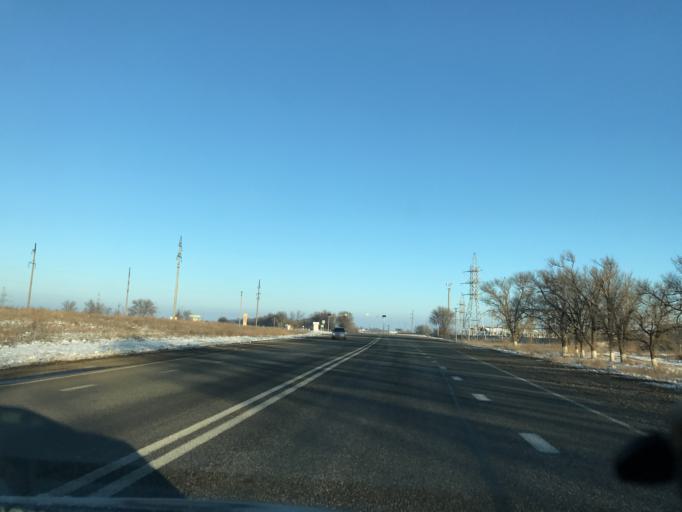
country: RU
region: Stavropol'skiy
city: Bezopasnoye
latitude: 45.6149
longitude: 41.9414
